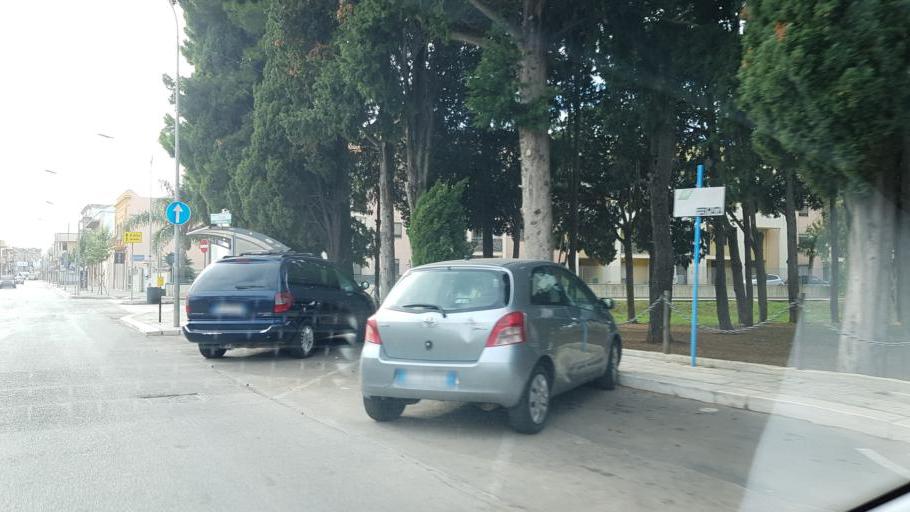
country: IT
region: Apulia
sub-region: Provincia di Brindisi
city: Mesagne
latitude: 40.5638
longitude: 17.8132
